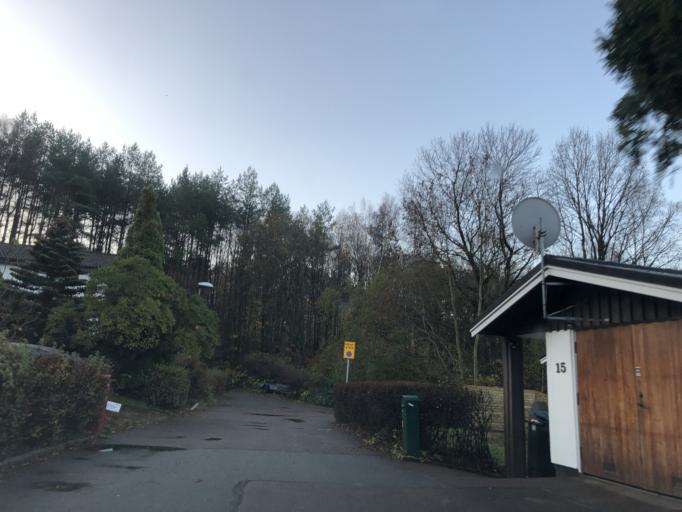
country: SE
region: Vaestra Goetaland
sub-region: Goteborg
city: Hammarkullen
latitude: 57.7878
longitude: 12.0322
